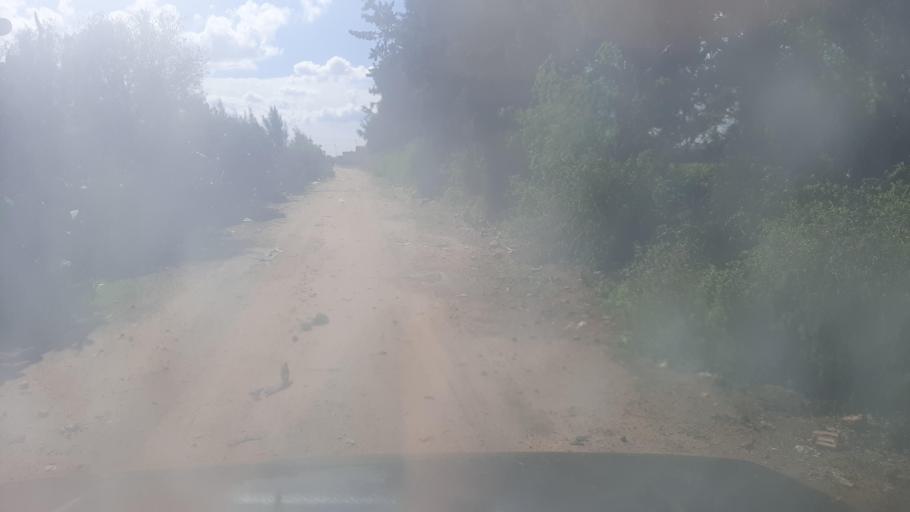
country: TN
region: Nabul
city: Korba
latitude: 36.6231
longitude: 10.8572
